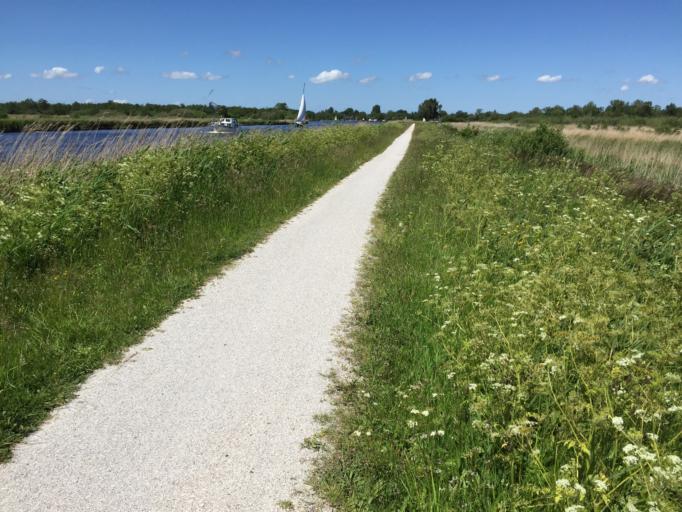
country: NL
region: Friesland
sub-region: Gemeente Smallingerland
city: Oudega
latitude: 53.1147
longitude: 5.9469
